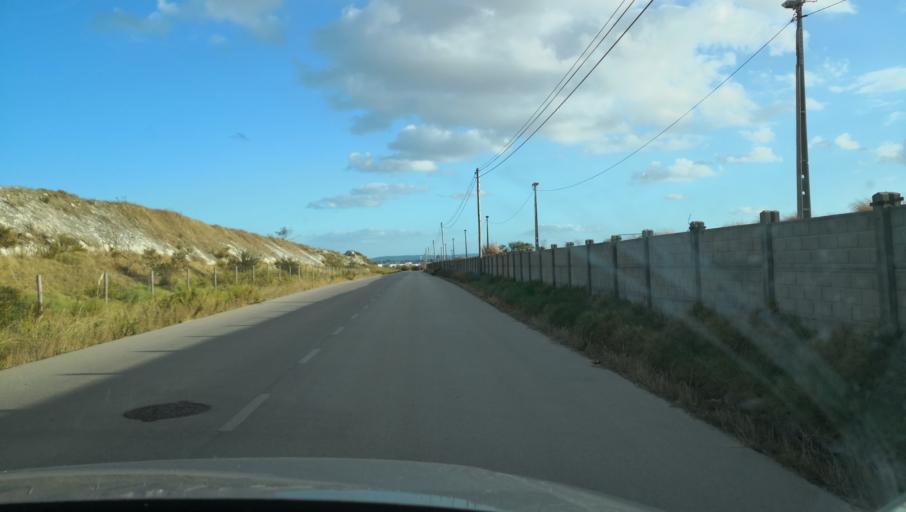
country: PT
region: Setubal
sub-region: Barreiro
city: Barreiro
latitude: 38.6739
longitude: -9.0459
